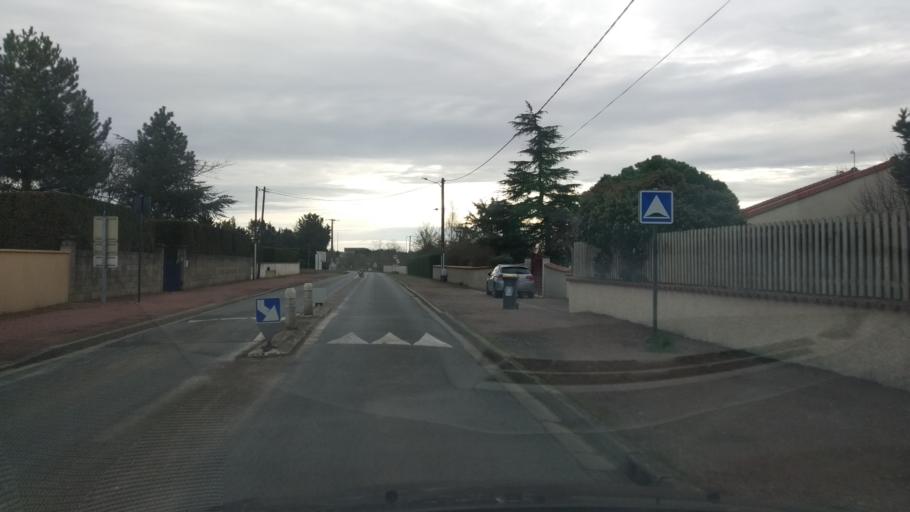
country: FR
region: Poitou-Charentes
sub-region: Departement de la Vienne
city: Dissay
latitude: 46.6888
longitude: 0.4163
